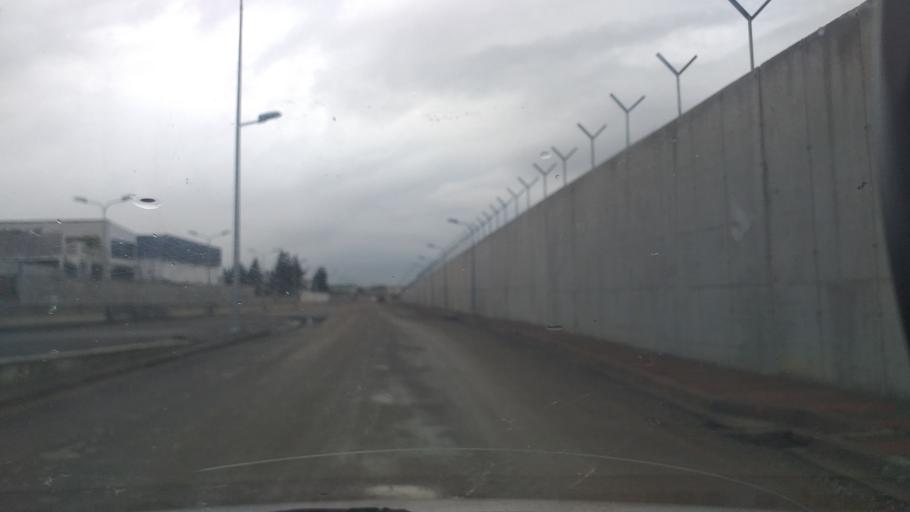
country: TN
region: Ariana
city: Ariana
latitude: 36.8531
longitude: 10.2125
